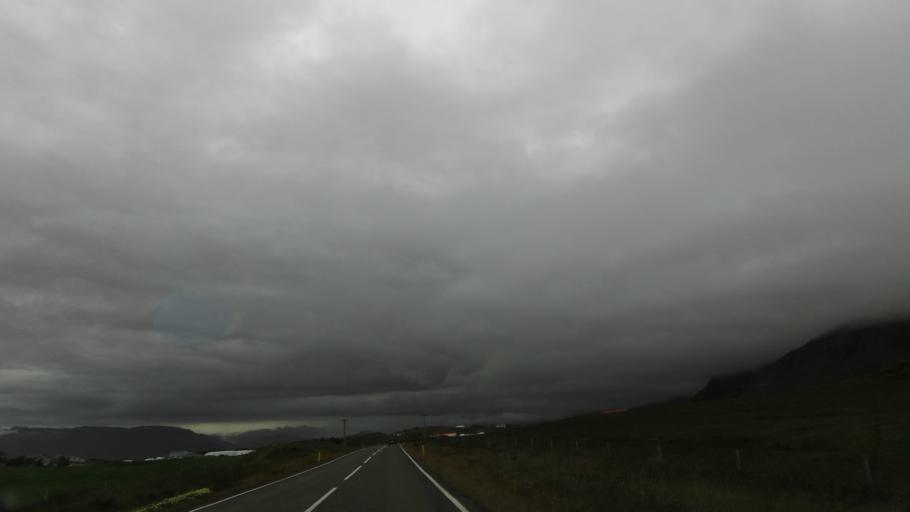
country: IS
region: East
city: Hoefn
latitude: 64.3167
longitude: -15.2354
